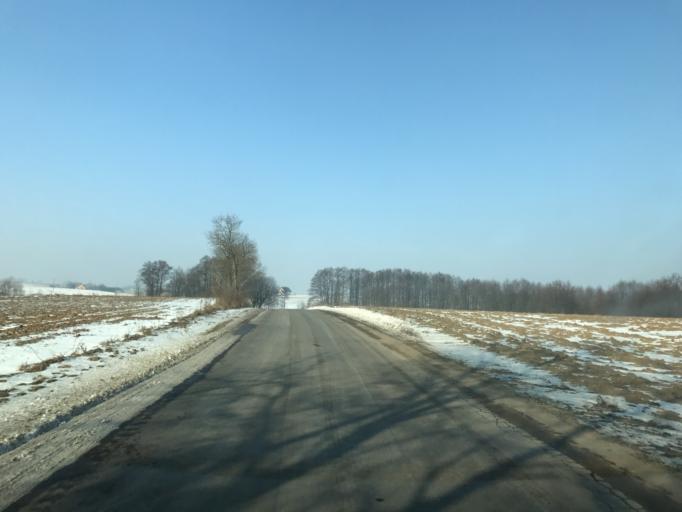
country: PL
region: Kujawsko-Pomorskie
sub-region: Powiat brodnicki
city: Swiedziebnia
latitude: 53.2042
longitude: 19.5460
